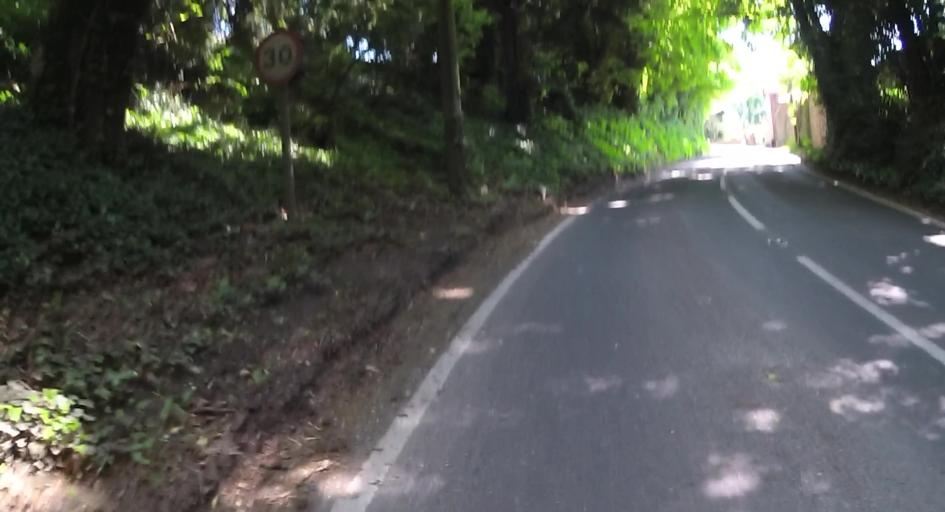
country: GB
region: England
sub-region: Hampshire
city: Four Marks
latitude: 51.1011
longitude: -1.1620
